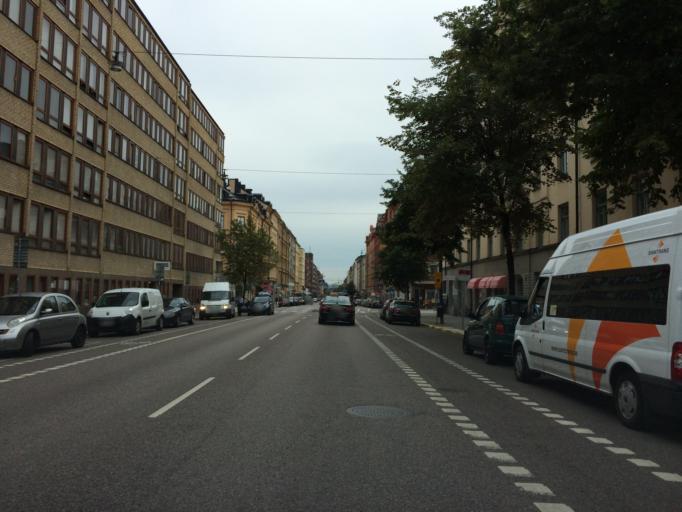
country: SE
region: Stockholm
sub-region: Solna Kommun
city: Solna
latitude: 59.3352
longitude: 18.0272
